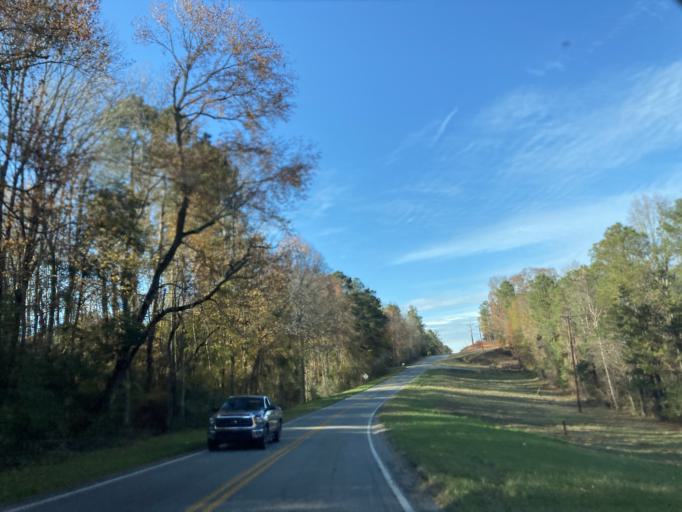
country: US
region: Georgia
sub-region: Jones County
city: Gray
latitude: 32.8991
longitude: -83.5204
